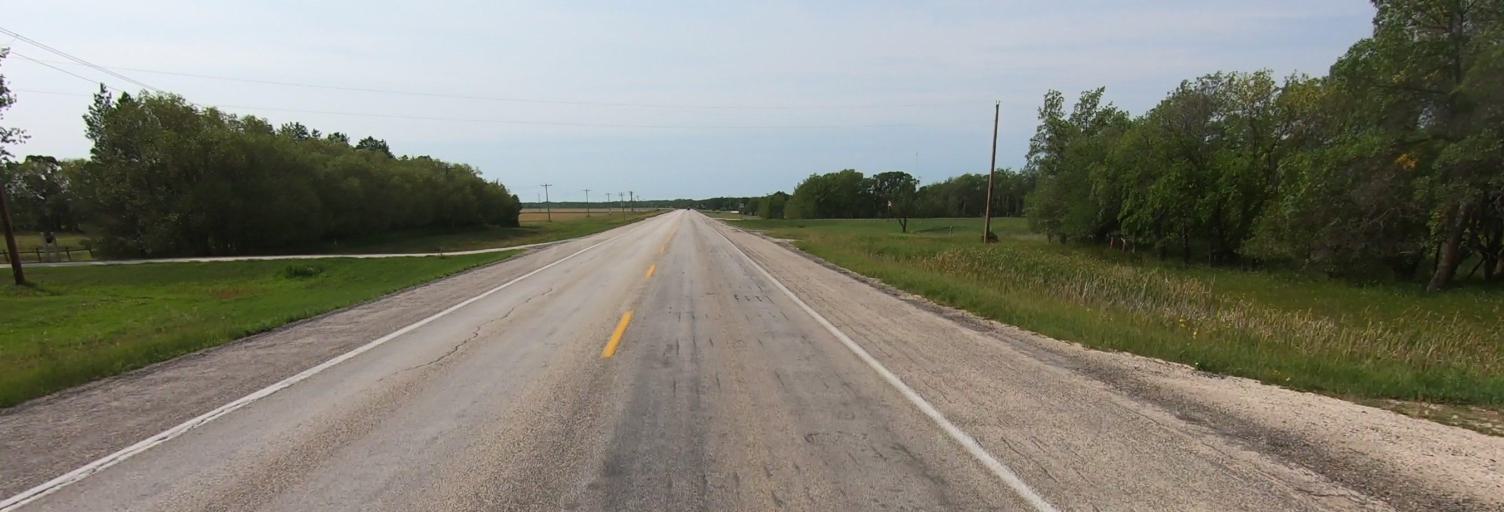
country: CA
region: Manitoba
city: Niverville
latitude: 49.6100
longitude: -97.1262
